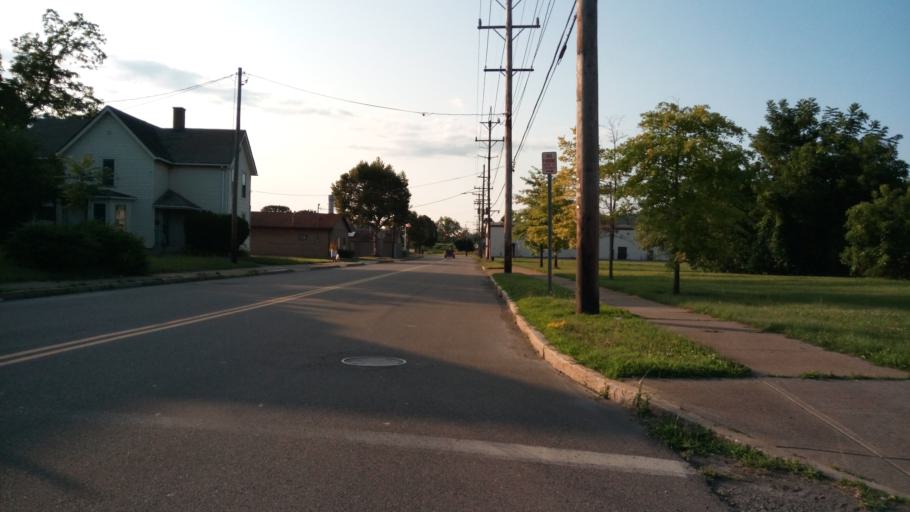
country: US
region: New York
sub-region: Chemung County
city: Elmira
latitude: 42.0932
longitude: -76.7907
